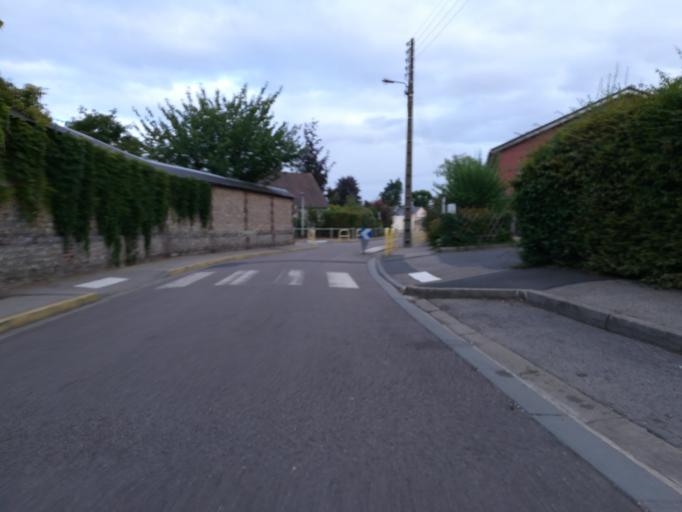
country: FR
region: Haute-Normandie
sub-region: Departement de la Seine-Maritime
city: Mont-Saint-Aignan
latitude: 49.4699
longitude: 1.0843
